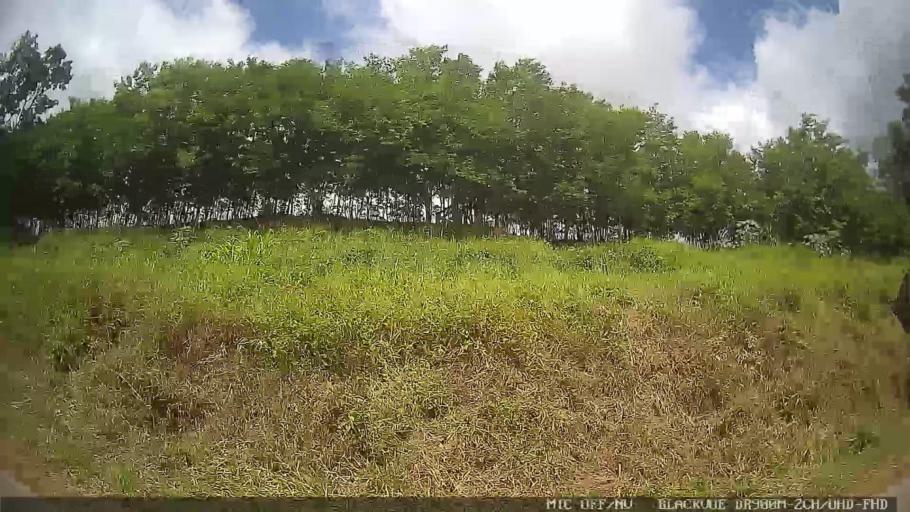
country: BR
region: Sao Paulo
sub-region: Braganca Paulista
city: Braganca Paulista
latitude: -22.8009
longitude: -46.5018
